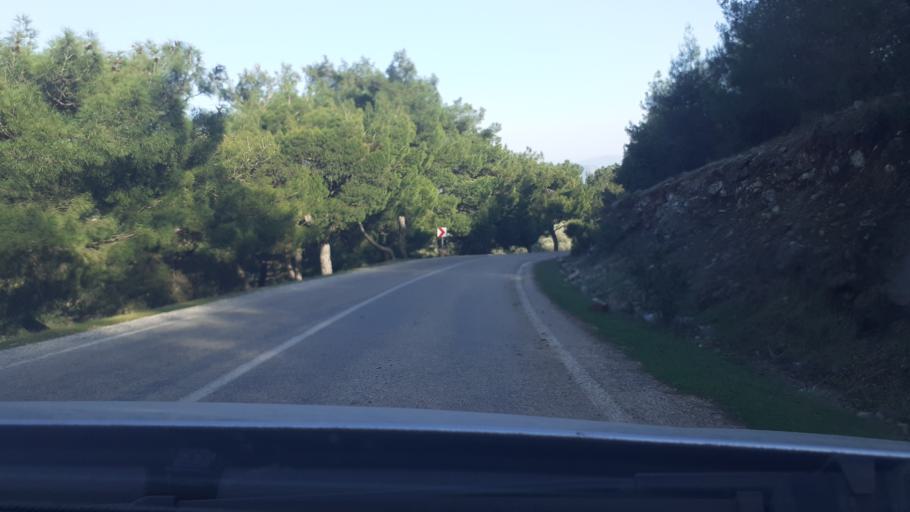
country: TR
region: Hatay
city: Aktepe
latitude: 36.7348
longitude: 36.4674
